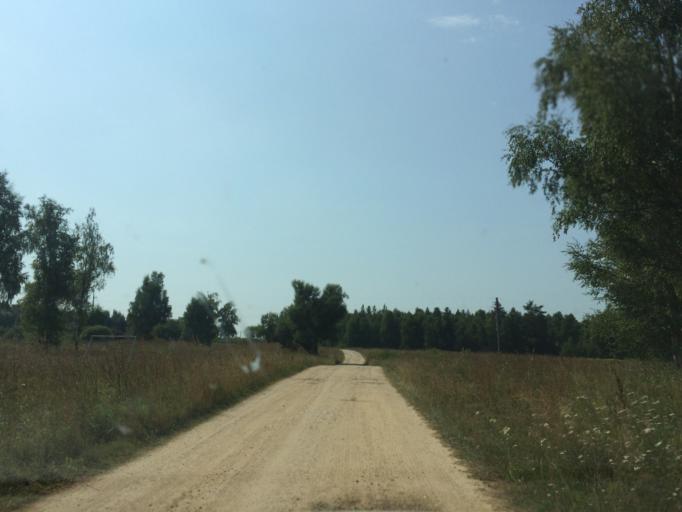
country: LV
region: Ludzas Rajons
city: Ludza
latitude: 56.5461
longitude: 27.5866
